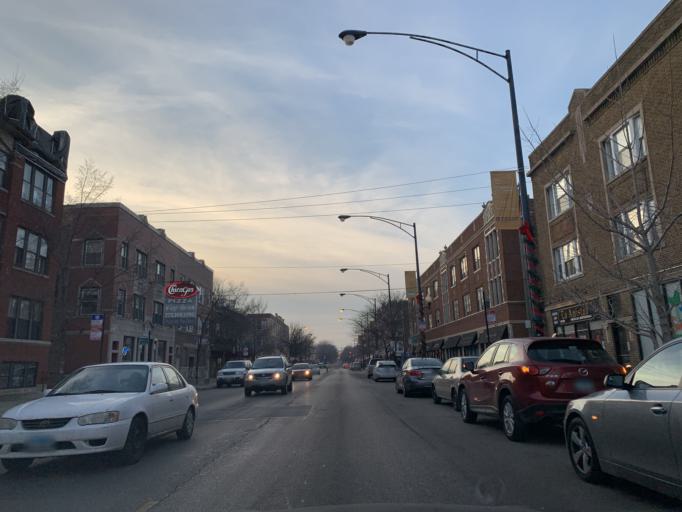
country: US
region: Illinois
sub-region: Cook County
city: Lincolnwood
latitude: 41.9615
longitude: -87.6765
